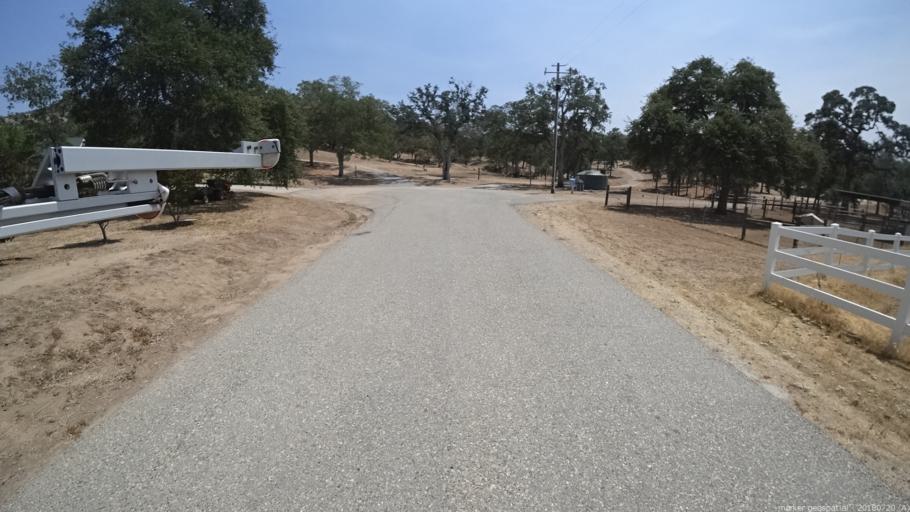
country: US
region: California
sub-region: Madera County
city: Yosemite Lakes
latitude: 37.2332
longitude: -119.7644
